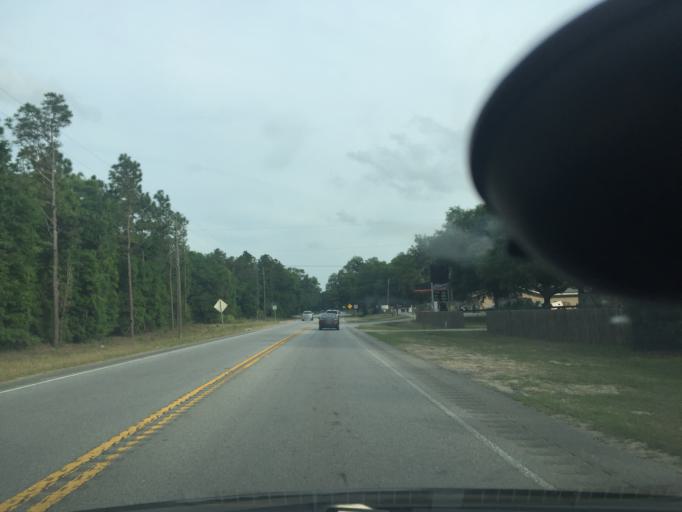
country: US
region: Georgia
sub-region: Bryan County
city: Richmond Hill
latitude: 32.0276
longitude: -81.3203
